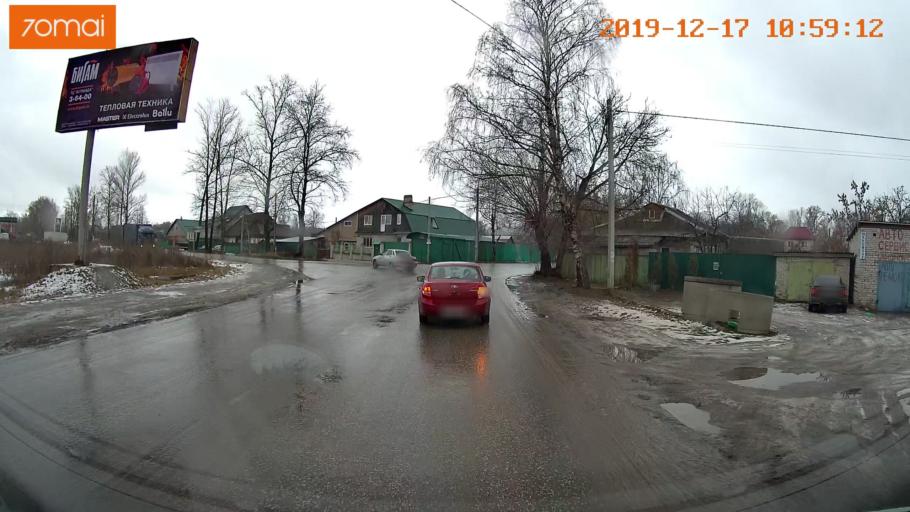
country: RU
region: Vladimir
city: Gus'-Khrustal'nyy
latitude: 55.6222
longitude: 40.6489
